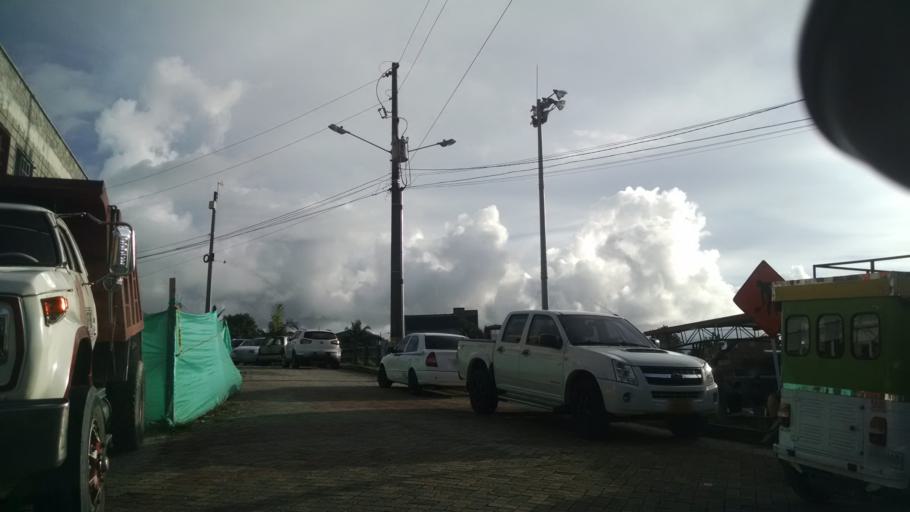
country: CO
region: Antioquia
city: Guatape
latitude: 6.2332
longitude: -75.1587
